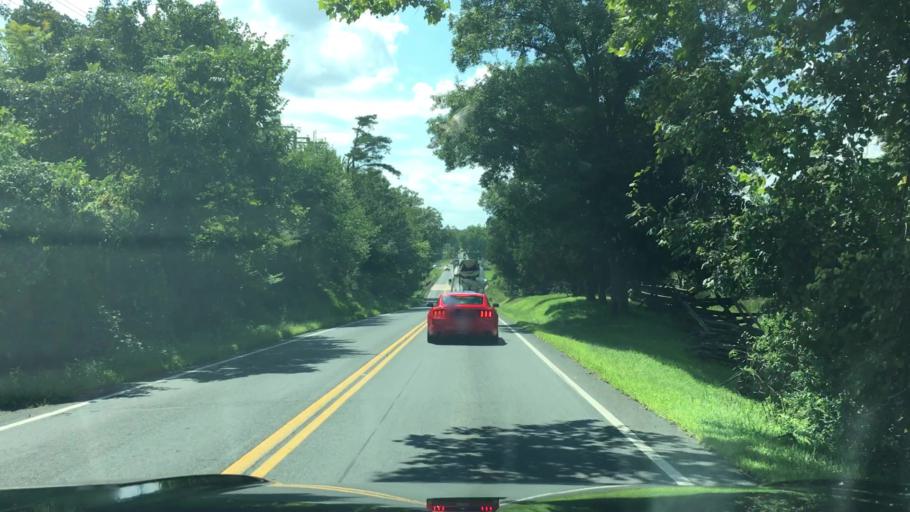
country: US
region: Virginia
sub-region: Prince William County
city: Bull Run
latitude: 38.8197
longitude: -77.5221
